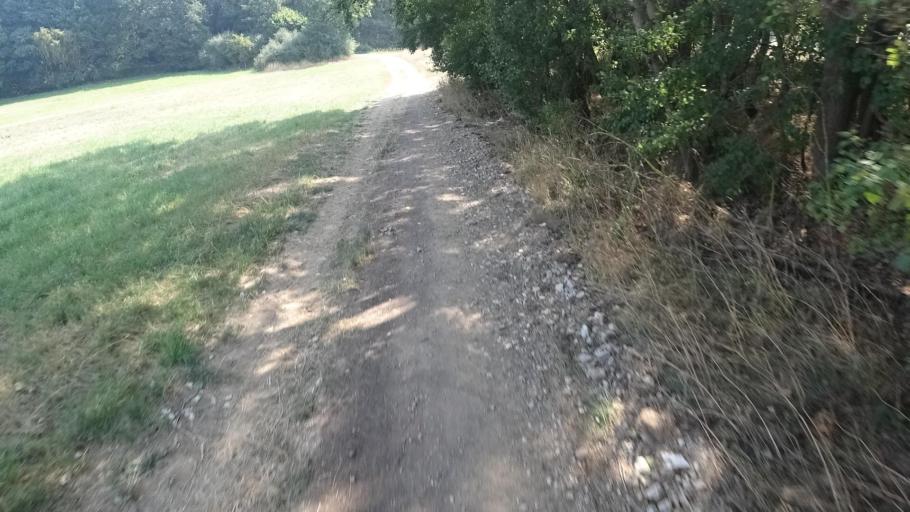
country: DE
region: Rheinland-Pfalz
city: Wahlbach
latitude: 49.9895
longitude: 7.5899
